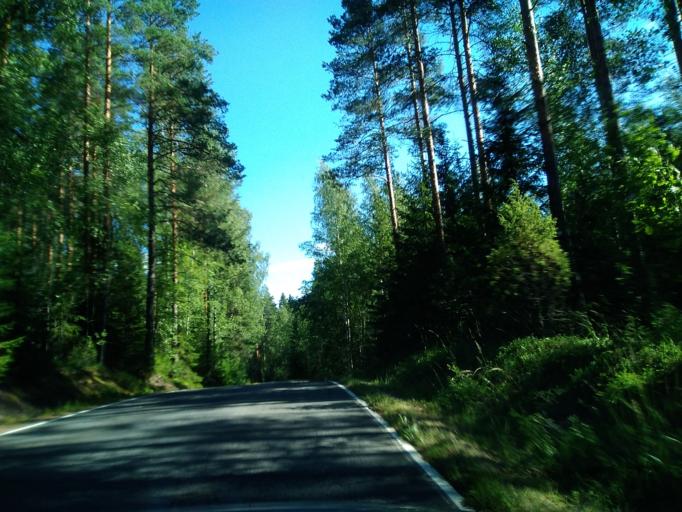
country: FI
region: Uusimaa
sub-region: Helsinki
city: Kaerkoelae
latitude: 60.7838
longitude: 24.0797
